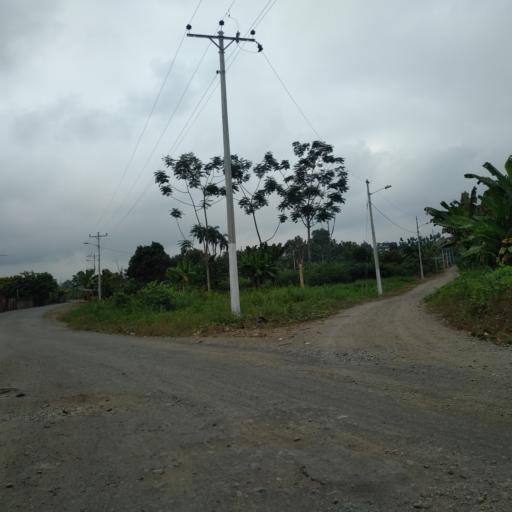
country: EC
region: Los Rios
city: Quevedo
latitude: -0.9741
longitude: -79.3564
